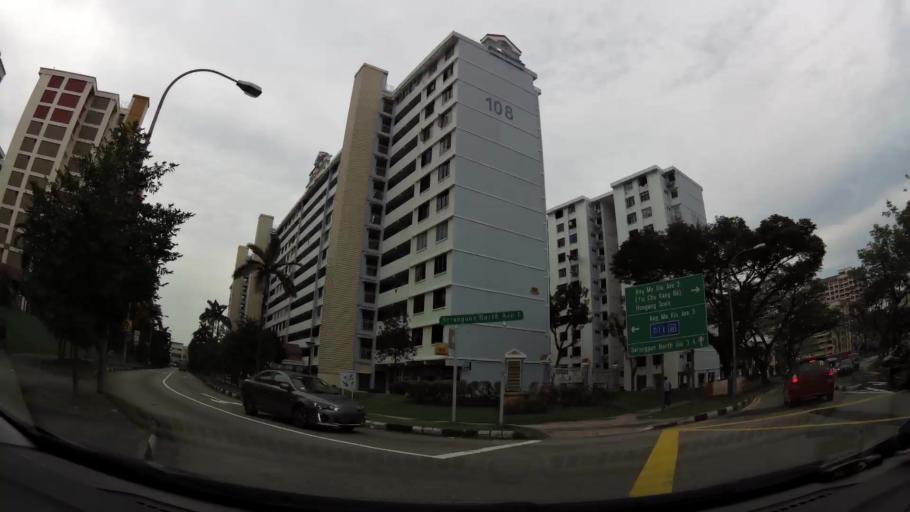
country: SG
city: Singapore
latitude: 1.3697
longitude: 103.8715
